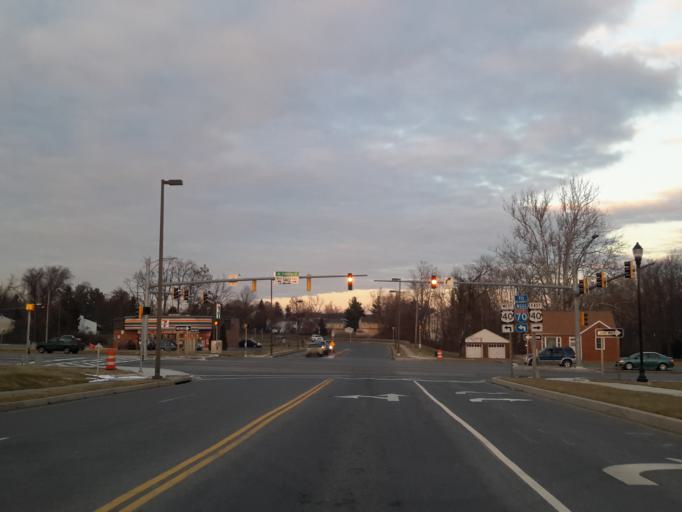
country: US
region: Maryland
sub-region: Frederick County
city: Braddock Heights
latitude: 39.4215
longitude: -77.4668
